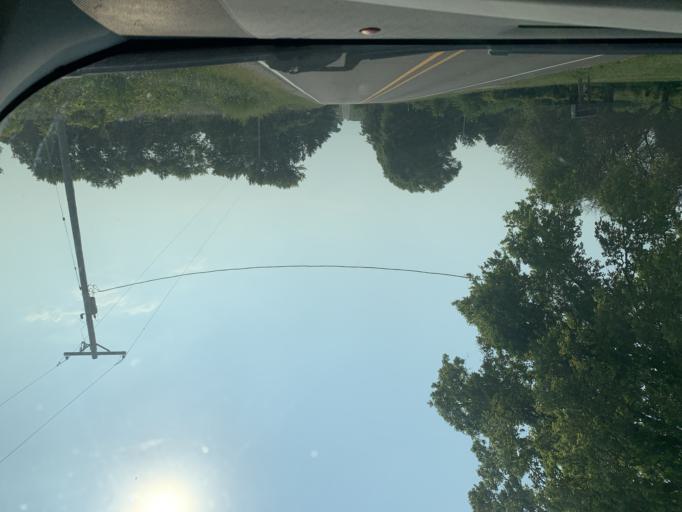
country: US
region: Illinois
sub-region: Whiteside County
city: Sterling
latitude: 41.8441
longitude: -89.7868
